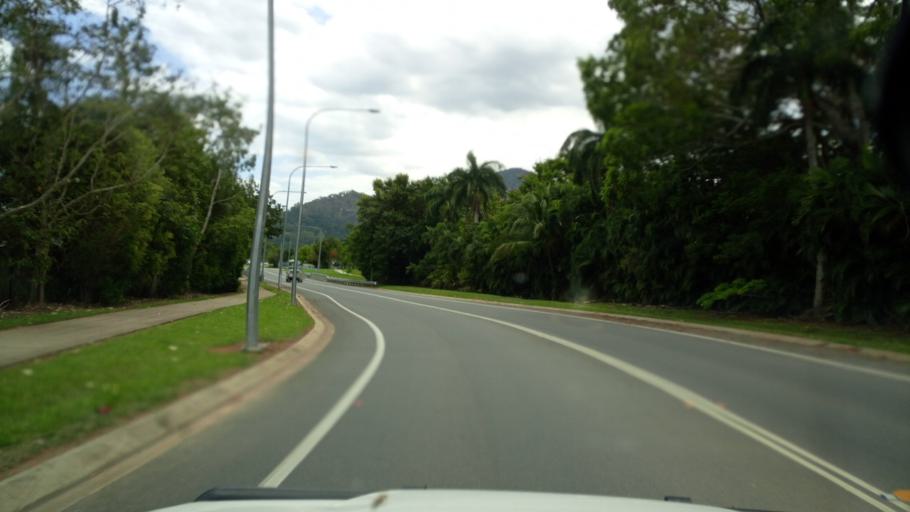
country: AU
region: Queensland
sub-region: Cairns
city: Redlynch
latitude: -16.8965
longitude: 145.6945
